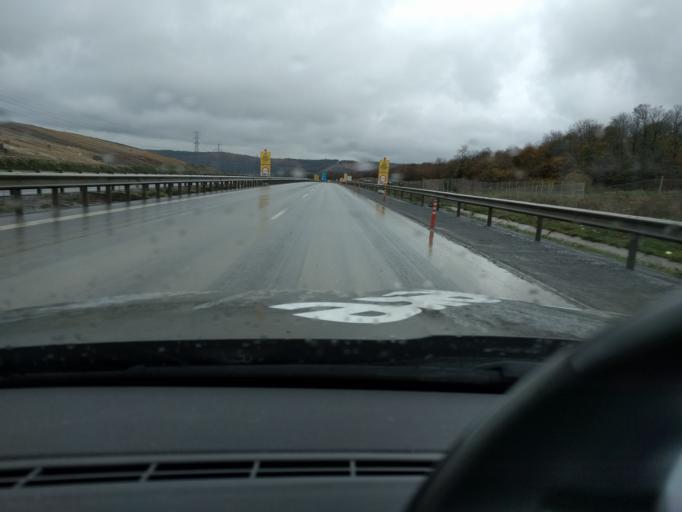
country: TR
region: Istanbul
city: Kemerburgaz
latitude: 41.2251
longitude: 28.8436
